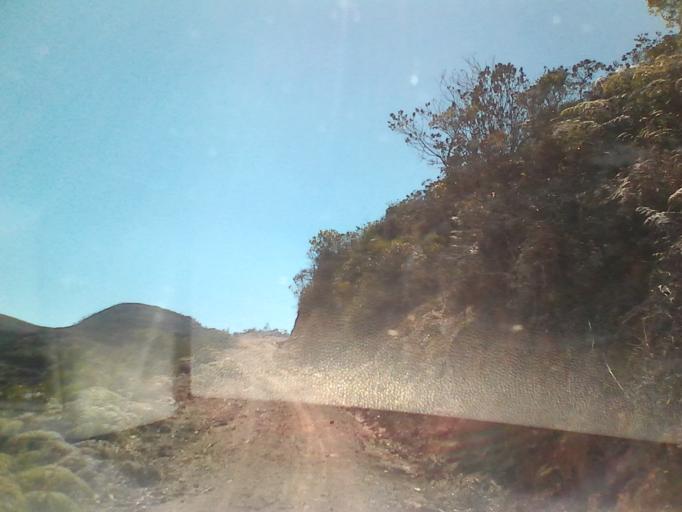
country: CO
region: Boyaca
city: Sachica
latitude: 5.5397
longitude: -73.5538
